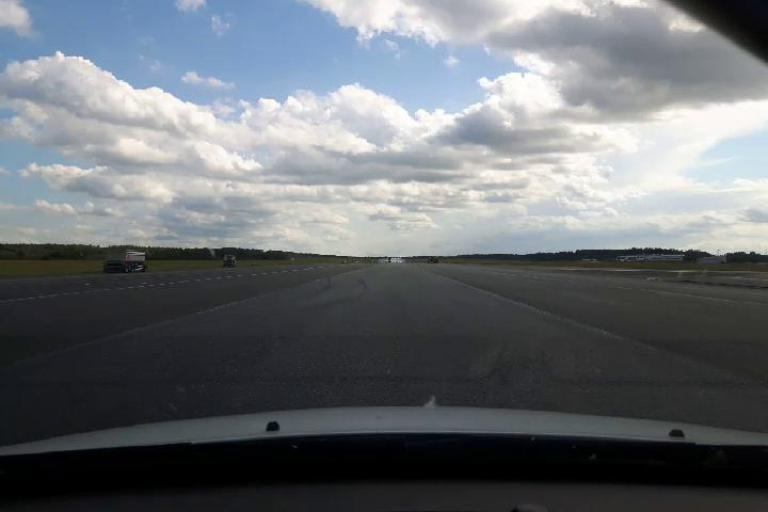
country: SE
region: Stockholm
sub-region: Sigtuna Kommun
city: Rosersberg
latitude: 59.6447
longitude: 17.9572
